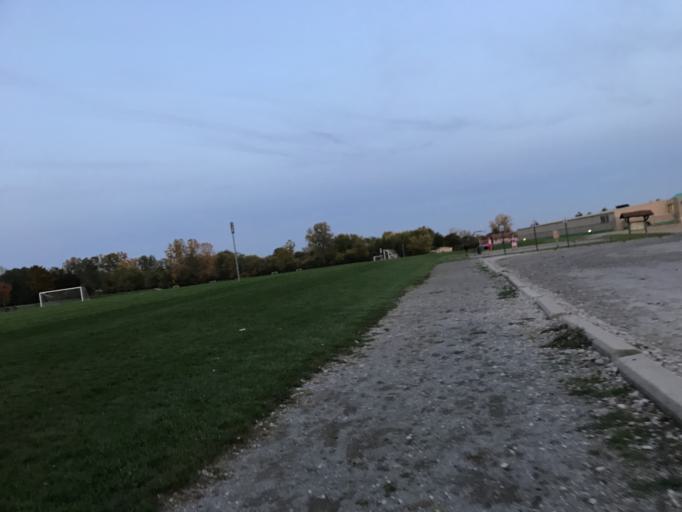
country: US
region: Michigan
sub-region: Oakland County
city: Farmington
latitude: 42.4420
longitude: -83.3980
